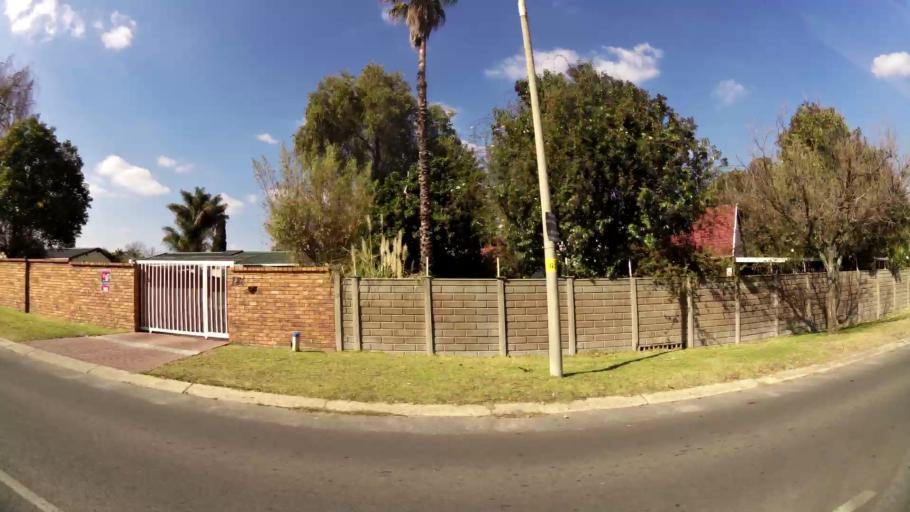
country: ZA
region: Gauteng
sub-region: Ekurhuleni Metropolitan Municipality
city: Tembisa
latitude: -26.0673
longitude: 28.2536
